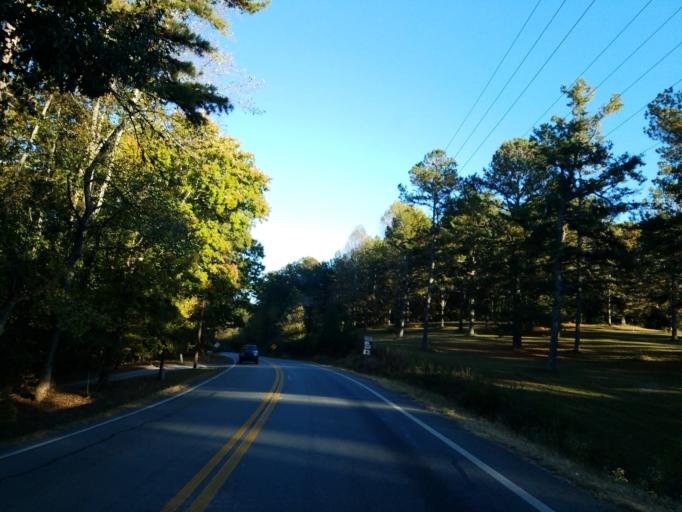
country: US
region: Georgia
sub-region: Dawson County
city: Dawsonville
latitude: 34.4271
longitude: -84.1577
